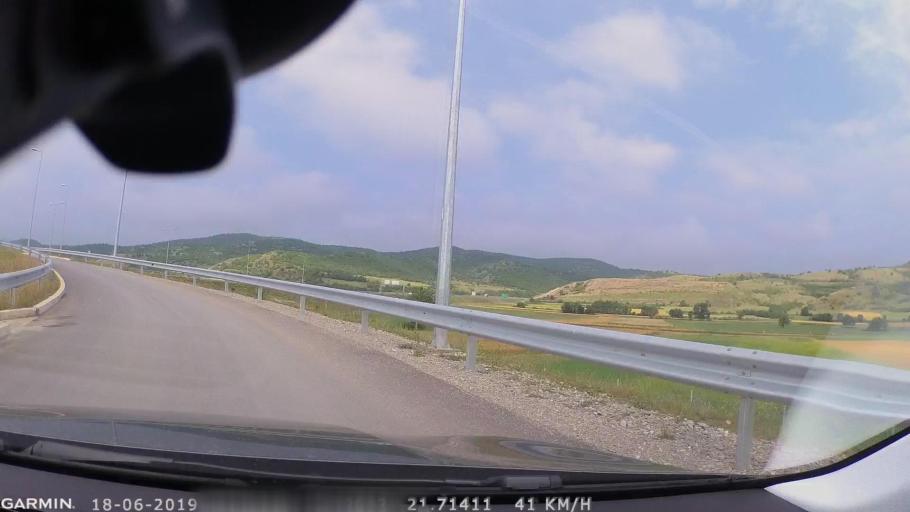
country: MK
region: Petrovec
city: Sredno Konjare
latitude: 41.9442
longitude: 21.8063
